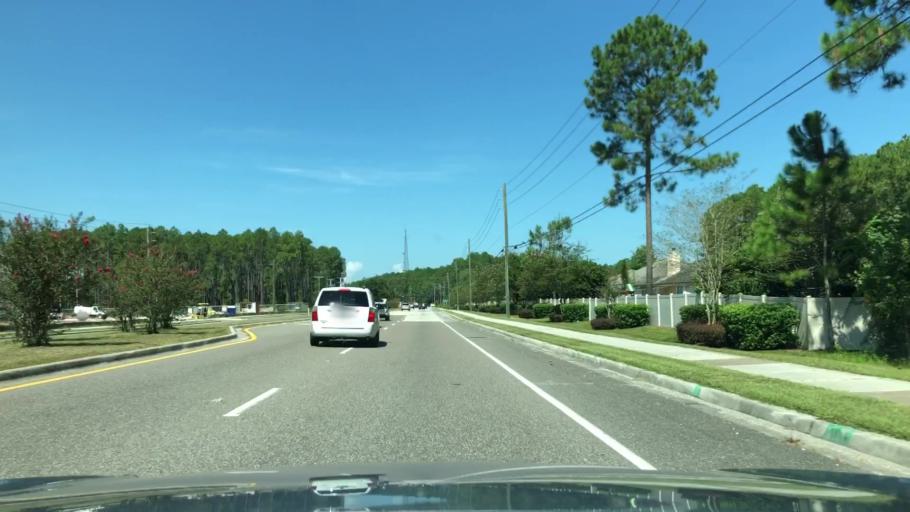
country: US
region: Florida
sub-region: Saint Johns County
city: Fruit Cove
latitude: 30.0601
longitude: -81.5259
